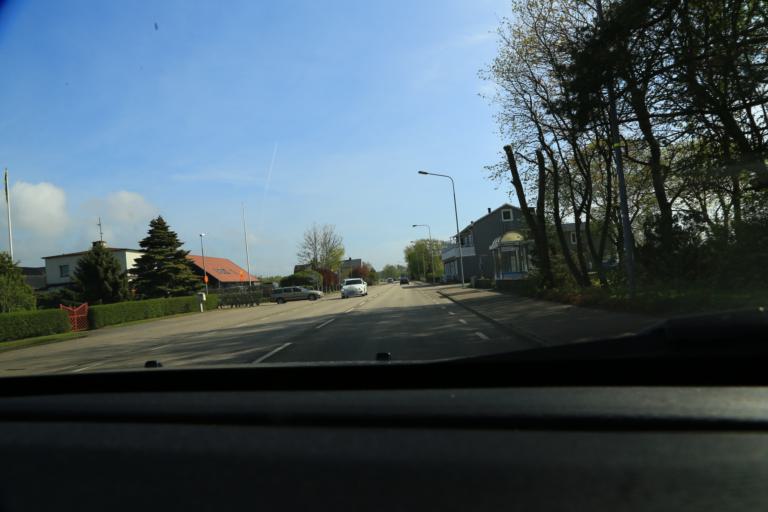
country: SE
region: Halland
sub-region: Varbergs Kommun
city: Veddige
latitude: 57.2200
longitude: 12.2217
